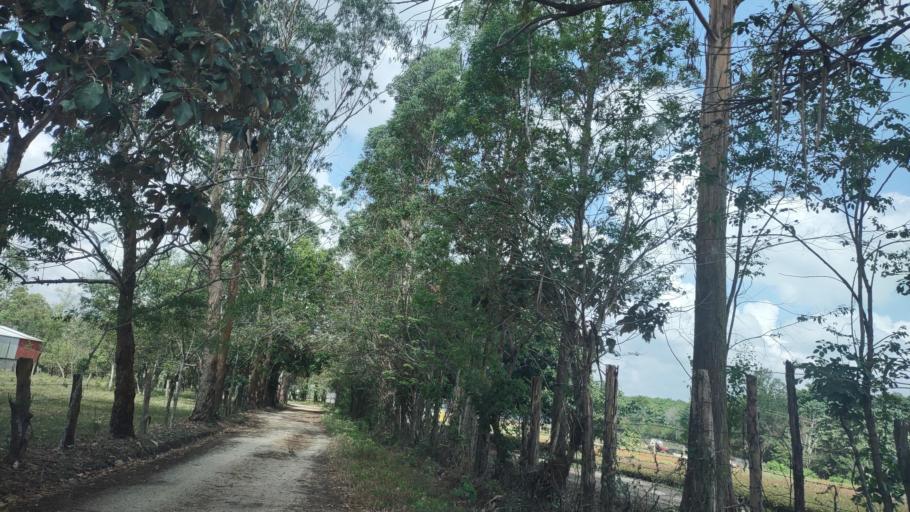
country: MX
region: Veracruz
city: Las Choapas
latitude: 17.9453
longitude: -94.1029
